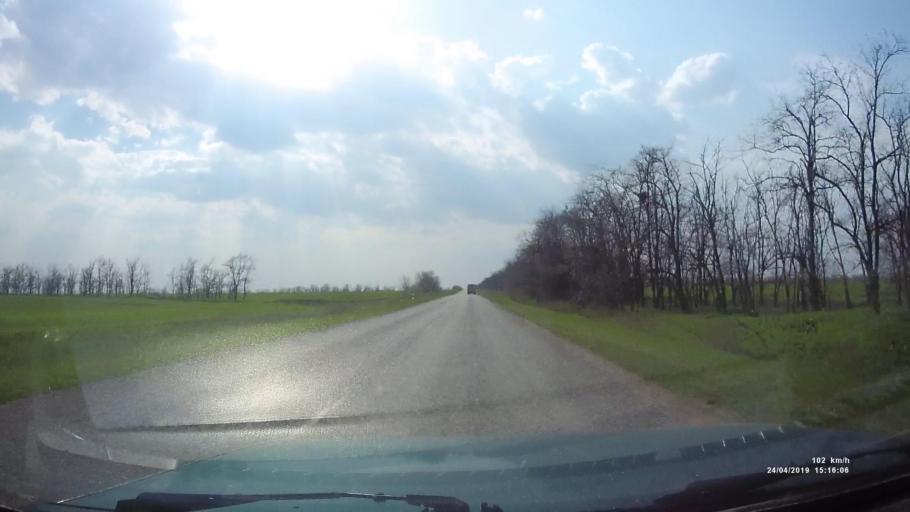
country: RU
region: Rostov
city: Remontnoye
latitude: 46.5469
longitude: 43.2203
